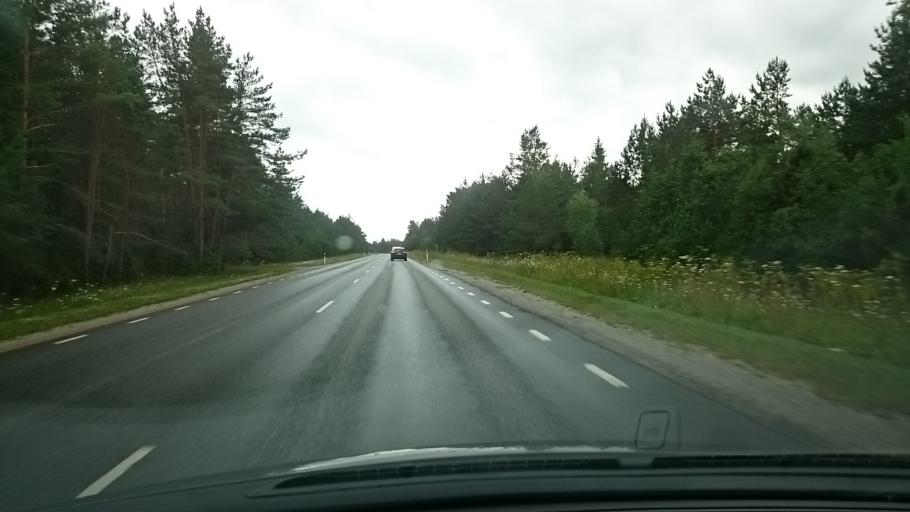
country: EE
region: Harju
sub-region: Keila linn
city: Keila
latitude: 59.2713
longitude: 24.2949
